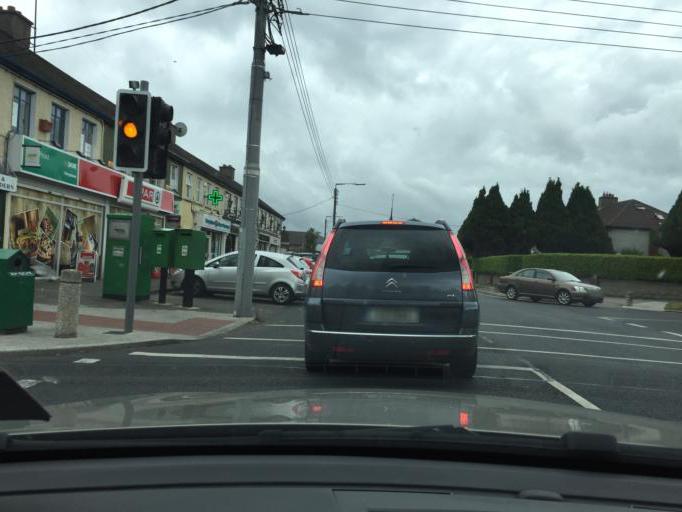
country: IE
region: Leinster
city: Templeogue
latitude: 53.3083
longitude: -6.3201
